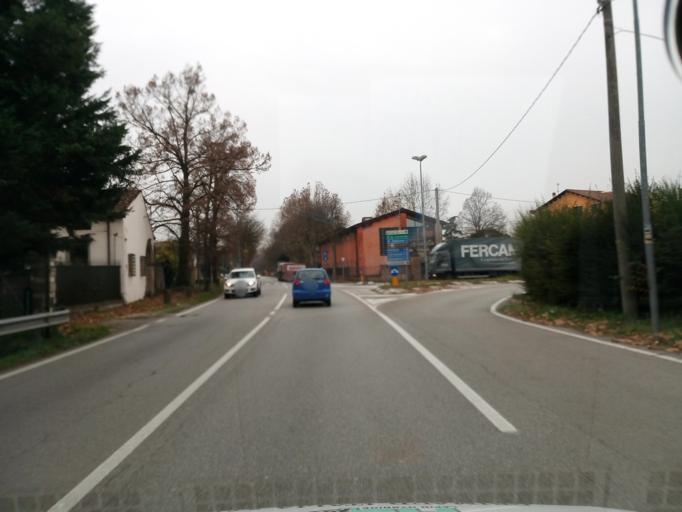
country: IT
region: Veneto
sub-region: Provincia di Padova
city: Vigonza
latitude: 45.4385
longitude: 11.9612
